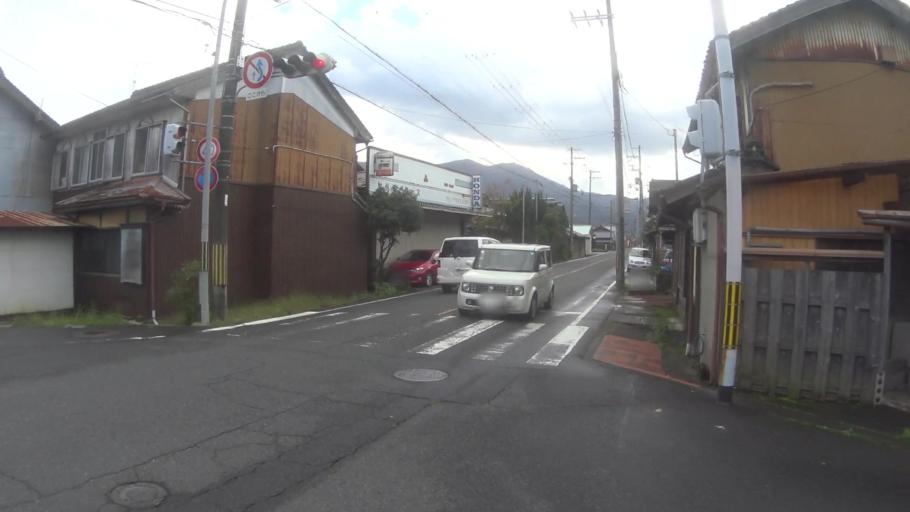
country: JP
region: Kyoto
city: Miyazu
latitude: 35.5036
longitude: 135.0937
